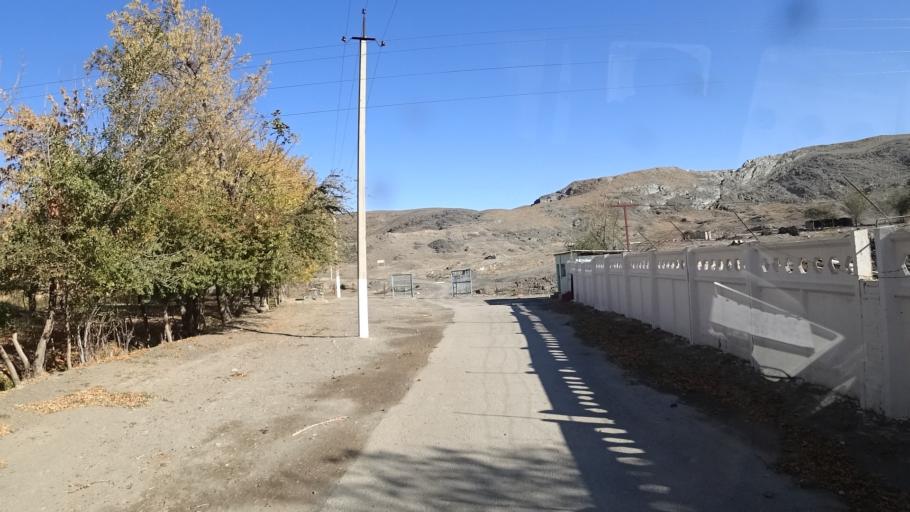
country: UZ
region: Navoiy
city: Nurota
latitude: 40.2968
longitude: 65.6055
